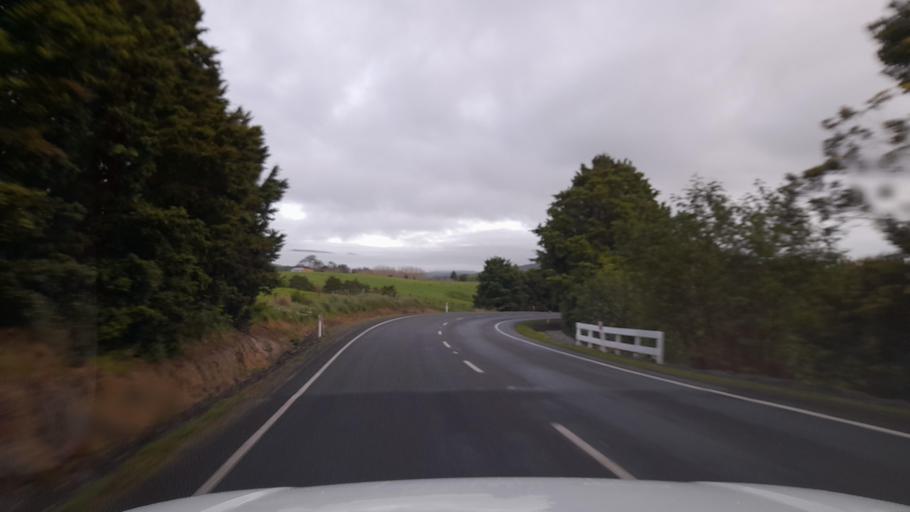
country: NZ
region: Northland
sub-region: Whangarei
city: Maungatapere
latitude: -35.7249
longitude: 174.0429
